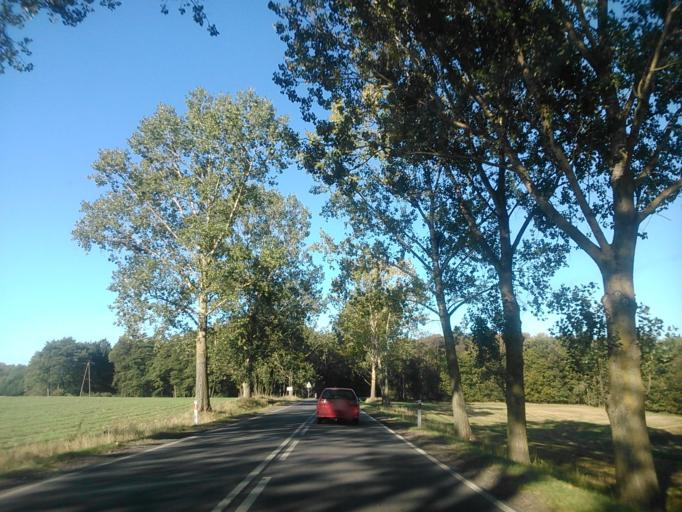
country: PL
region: Kujawsko-Pomorskie
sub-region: Powiat wabrzeski
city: Wabrzezno
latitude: 53.2574
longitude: 19.0146
